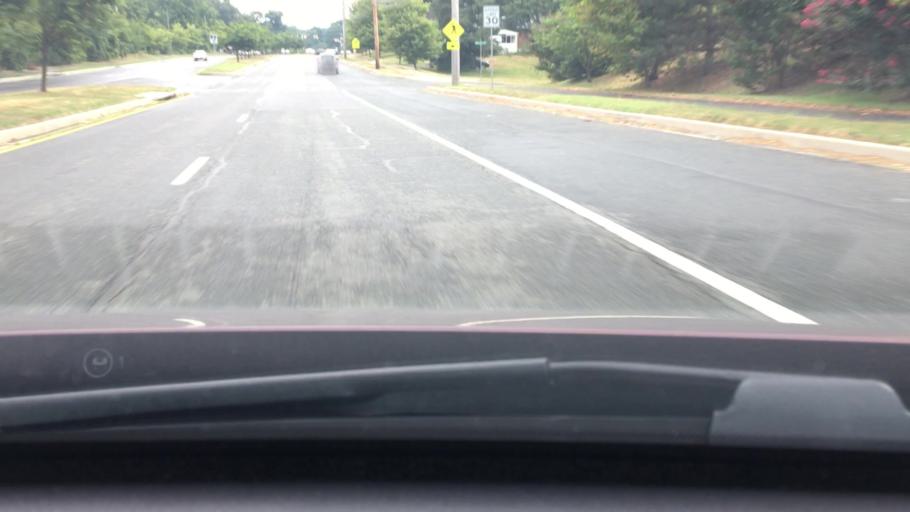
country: US
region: Maryland
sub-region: Prince George's County
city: Calverton
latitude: 39.0556
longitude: -76.9224
